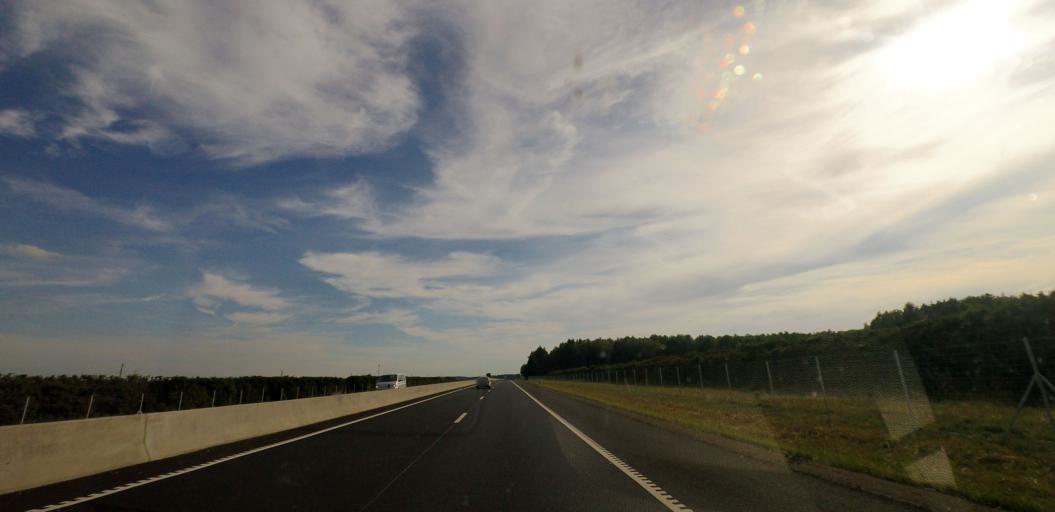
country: BY
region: Grodnenskaya
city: Lida
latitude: 53.7560
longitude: 25.0321
